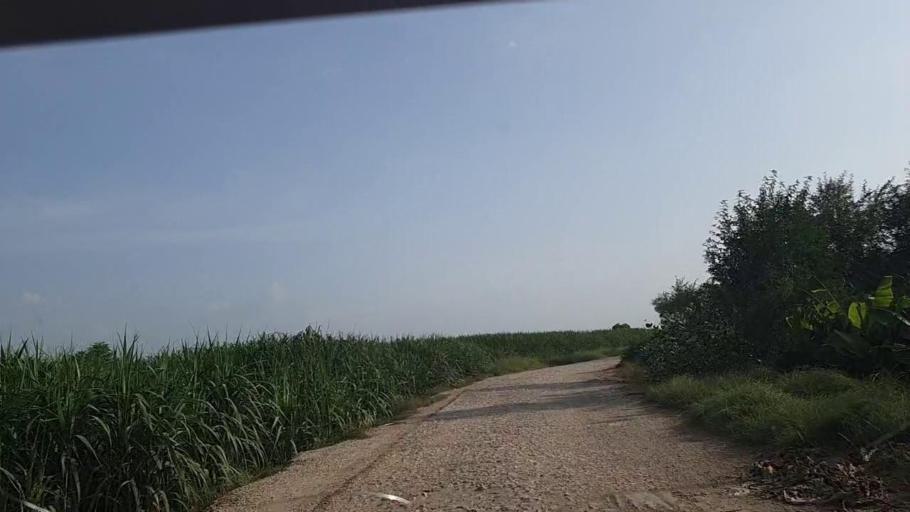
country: PK
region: Sindh
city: Ghotki
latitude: 27.9901
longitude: 69.2621
